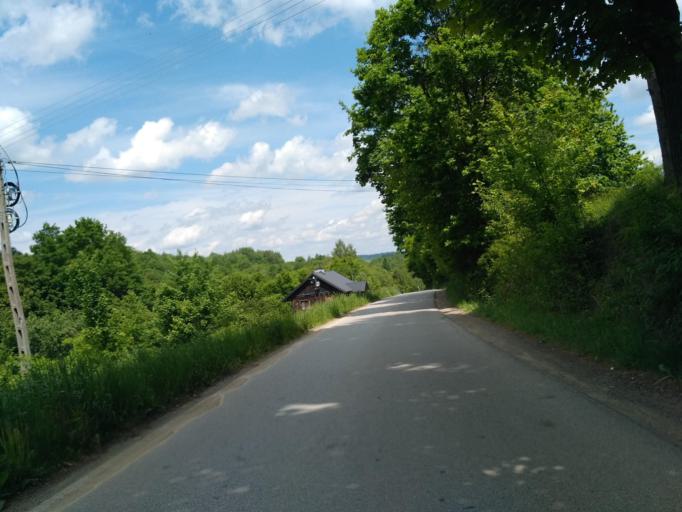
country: PL
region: Subcarpathian Voivodeship
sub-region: Powiat krosnienski
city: Dukla
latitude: 49.5737
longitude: 21.6183
